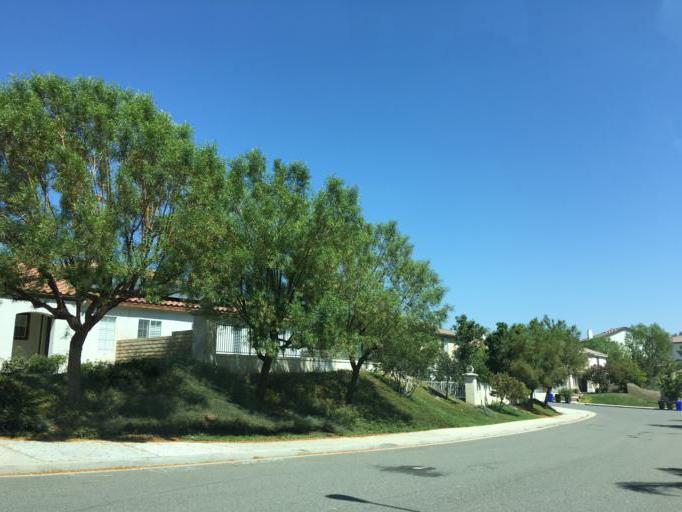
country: US
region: California
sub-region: Los Angeles County
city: Santa Clarita
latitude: 34.3843
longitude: -118.5986
